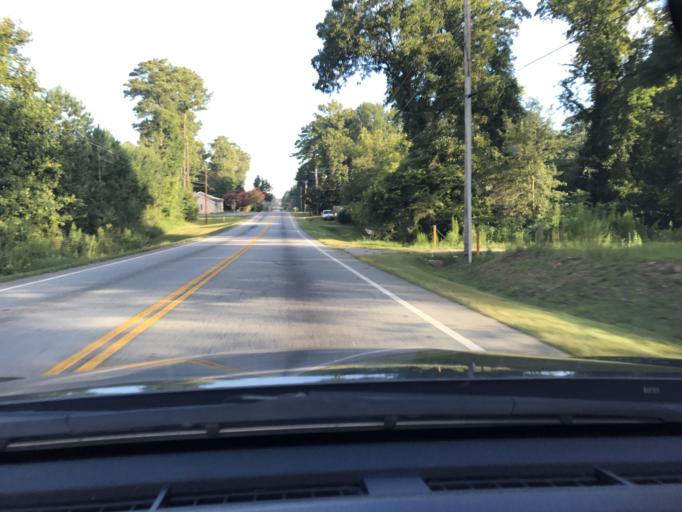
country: US
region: Georgia
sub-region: Clayton County
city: Lake City
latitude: 33.6019
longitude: -84.2995
